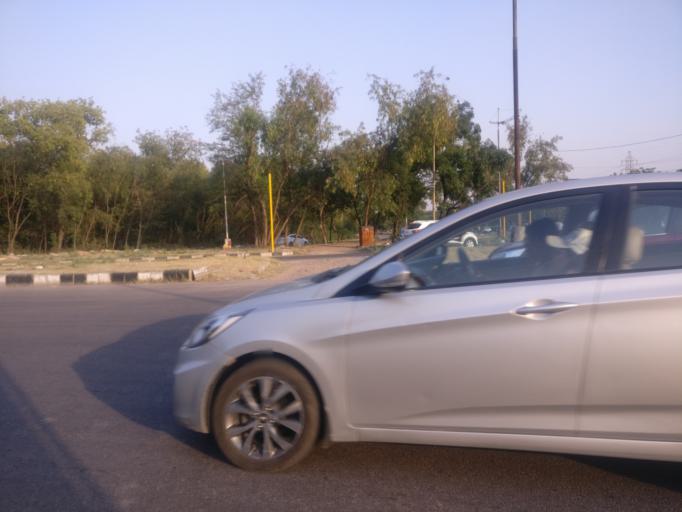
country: IN
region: Punjab
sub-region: Ajitgarh
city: Mohali
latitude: 30.7313
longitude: 76.7314
